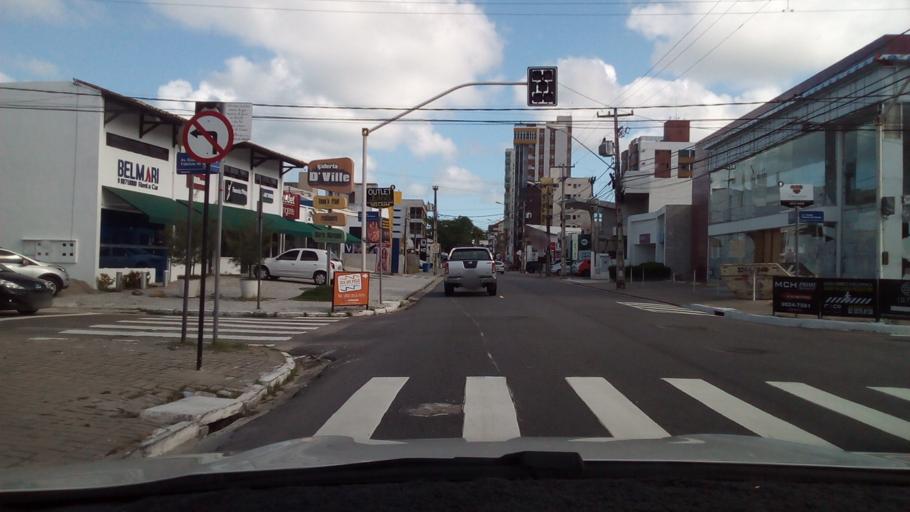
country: BR
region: Paraiba
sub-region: Joao Pessoa
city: Joao Pessoa
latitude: -7.1009
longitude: -34.8338
